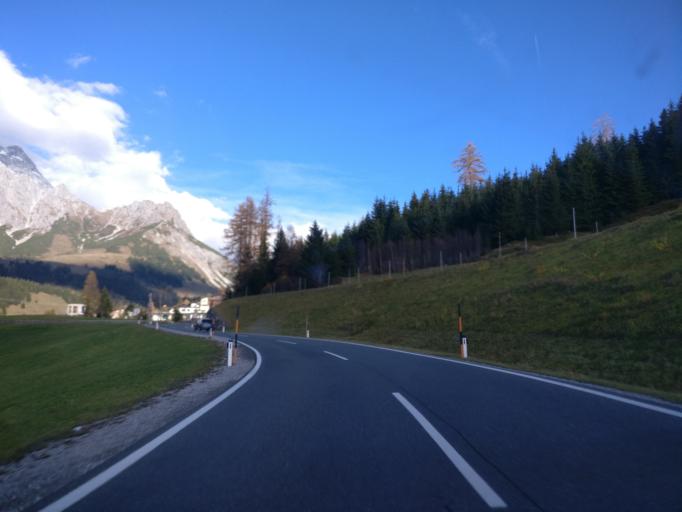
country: AT
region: Salzburg
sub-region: Politischer Bezirk Zell am See
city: Dienten am Hochkonig
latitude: 47.3870
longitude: 13.0237
